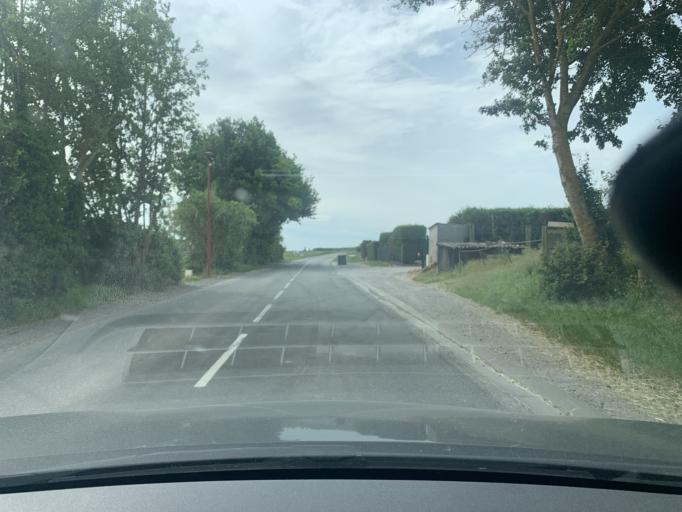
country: FR
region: Nord-Pas-de-Calais
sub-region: Departement du Nord
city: Marcoing
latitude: 50.1349
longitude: 3.1827
